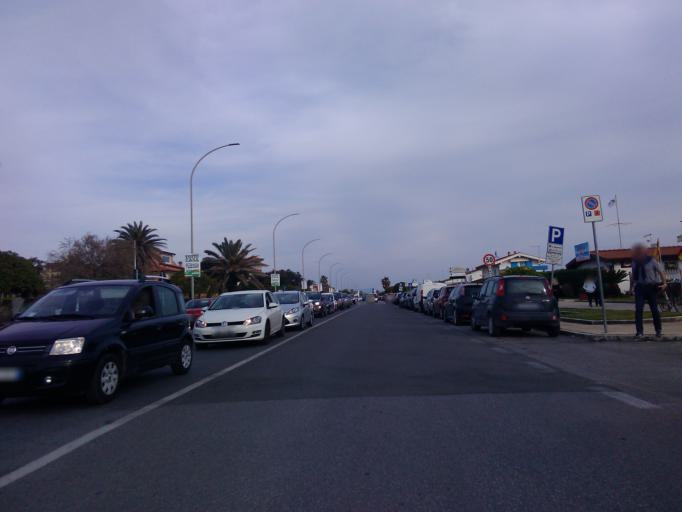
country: IT
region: Tuscany
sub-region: Provincia di Massa-Carrara
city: Massa
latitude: 44.0075
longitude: 10.0995
